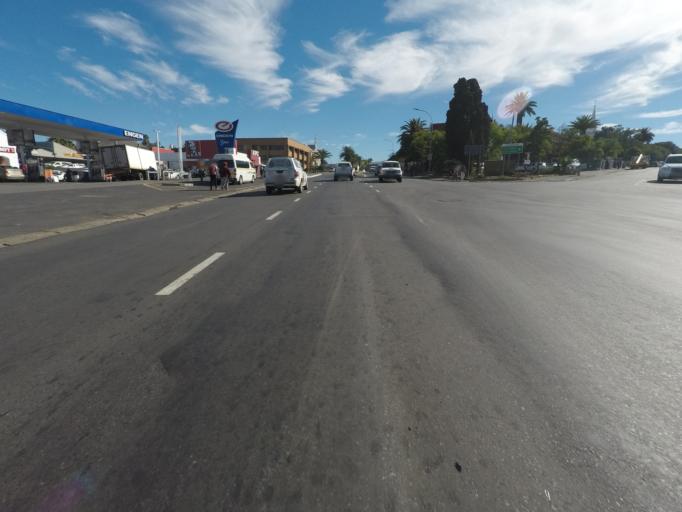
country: ZA
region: Western Cape
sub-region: West Coast District Municipality
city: Malmesbury
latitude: -33.4649
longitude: 18.7290
